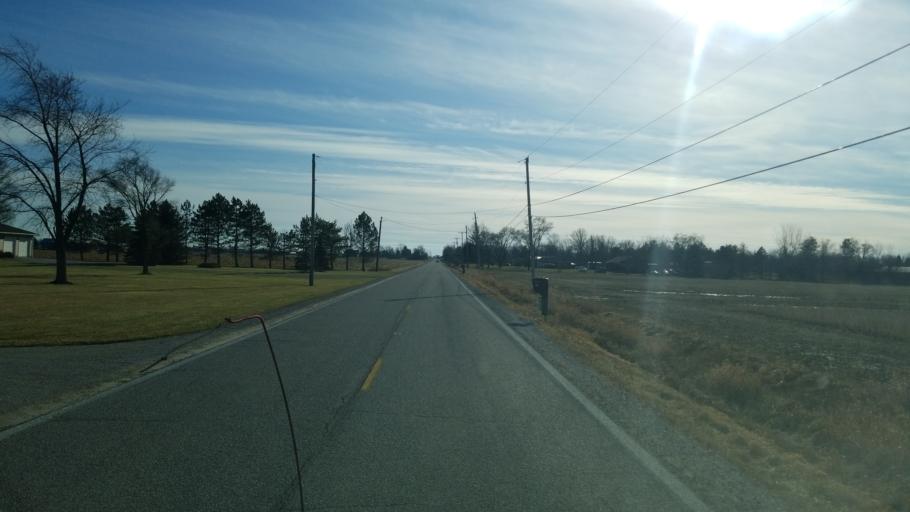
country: US
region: Ohio
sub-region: Sandusky County
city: Stony Prairie
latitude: 41.3679
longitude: -83.2229
